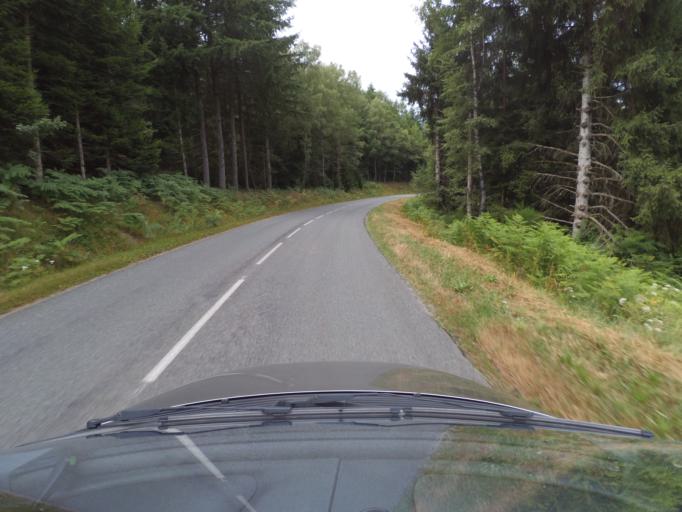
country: FR
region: Limousin
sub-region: Departement de la Haute-Vienne
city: Peyrat-le-Chateau
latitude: 45.8838
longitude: 1.8913
